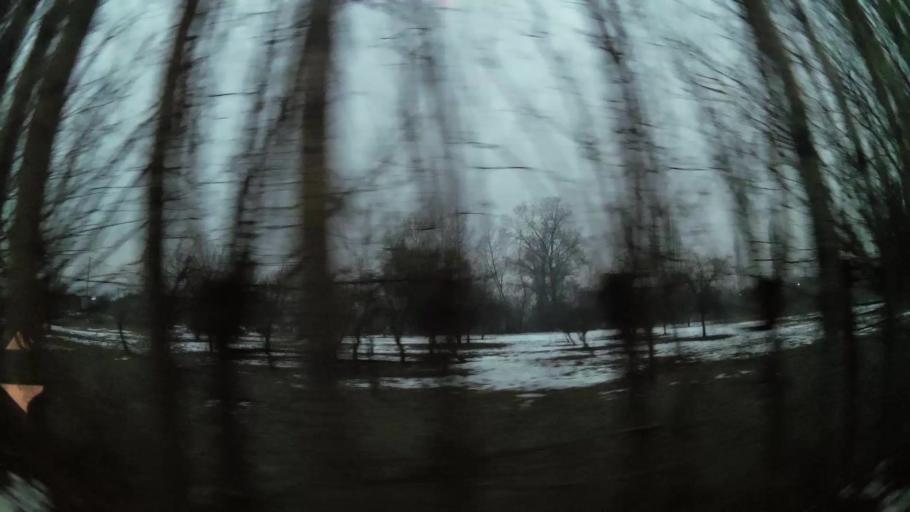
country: MK
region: Kisela Voda
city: Kisela Voda
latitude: 41.9726
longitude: 21.4916
